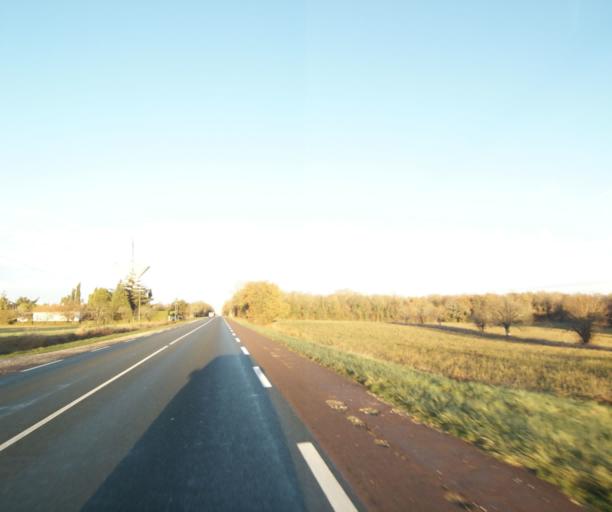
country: FR
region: Poitou-Charentes
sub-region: Departement de la Charente-Maritime
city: Saint-Georges-des-Coteaux
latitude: 45.7686
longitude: -0.6830
